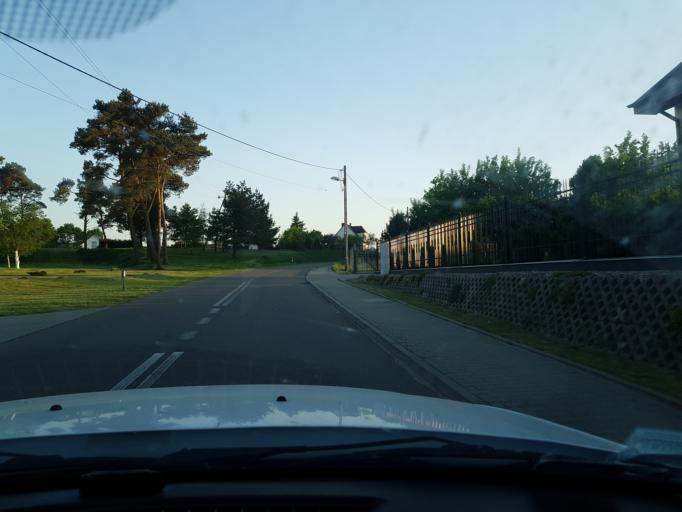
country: PL
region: West Pomeranian Voivodeship
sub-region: Powiat stargardzki
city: Kobylanka
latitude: 53.3561
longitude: 14.8529
